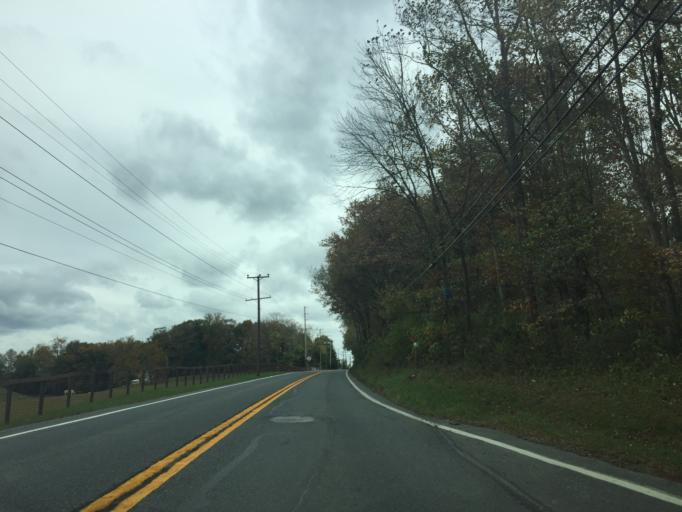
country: US
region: Maryland
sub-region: Harford County
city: Riverside
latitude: 39.5310
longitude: -76.2624
